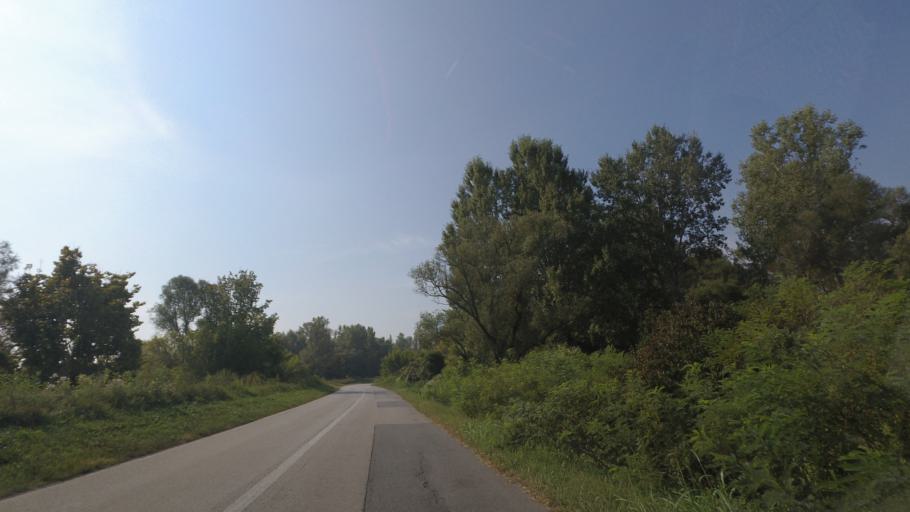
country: BA
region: Republika Srpska
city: Bosanska Dubica
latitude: 45.2563
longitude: 16.8813
